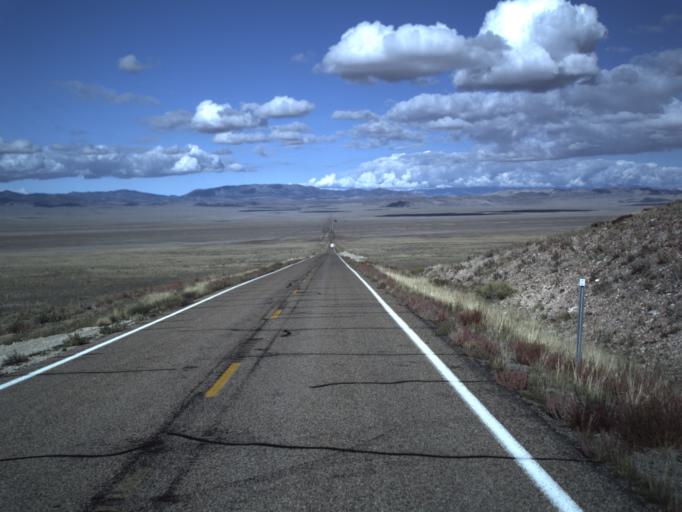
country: US
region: Utah
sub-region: Beaver County
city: Milford
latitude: 38.5095
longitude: -113.6201
